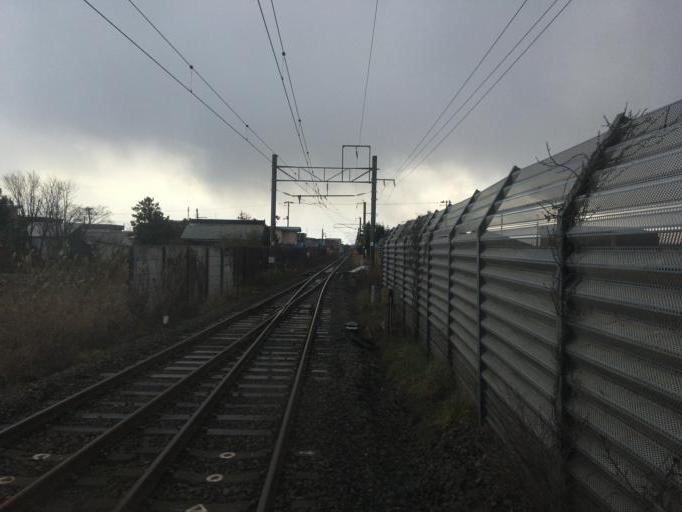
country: JP
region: Aomori
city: Aomori Shi
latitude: 40.8991
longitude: 140.6730
